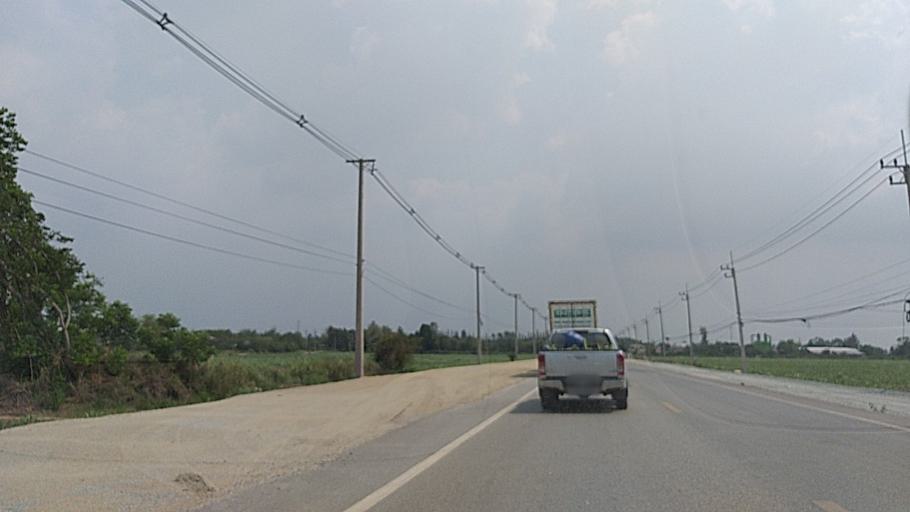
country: TH
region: Chon Buri
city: Phanat Nikhom
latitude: 13.3677
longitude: 101.1959
